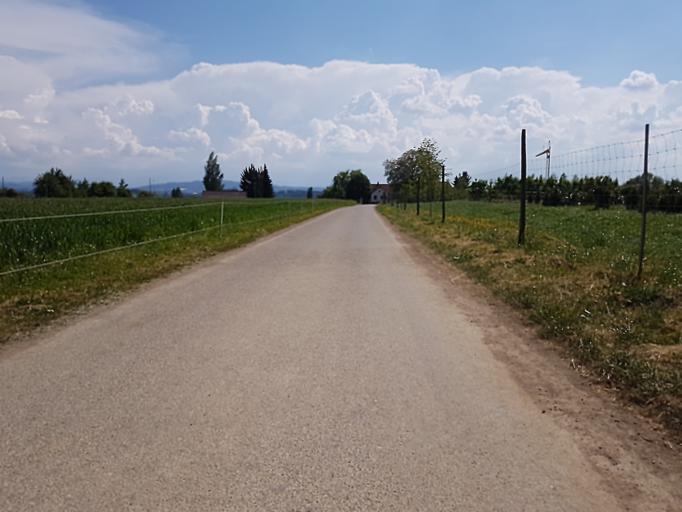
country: CH
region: Thurgau
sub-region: Arbon District
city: Amriswil
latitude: 47.5675
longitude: 9.3006
